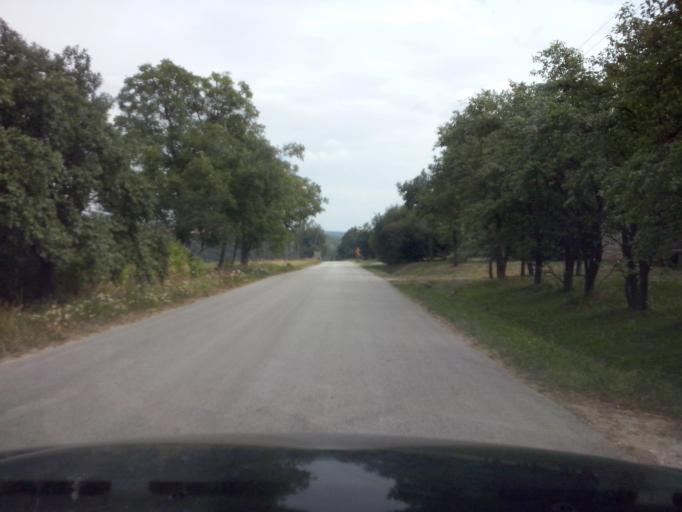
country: PL
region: Swietokrzyskie
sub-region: Powiat kielecki
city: Lagow
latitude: 50.7183
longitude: 21.1331
